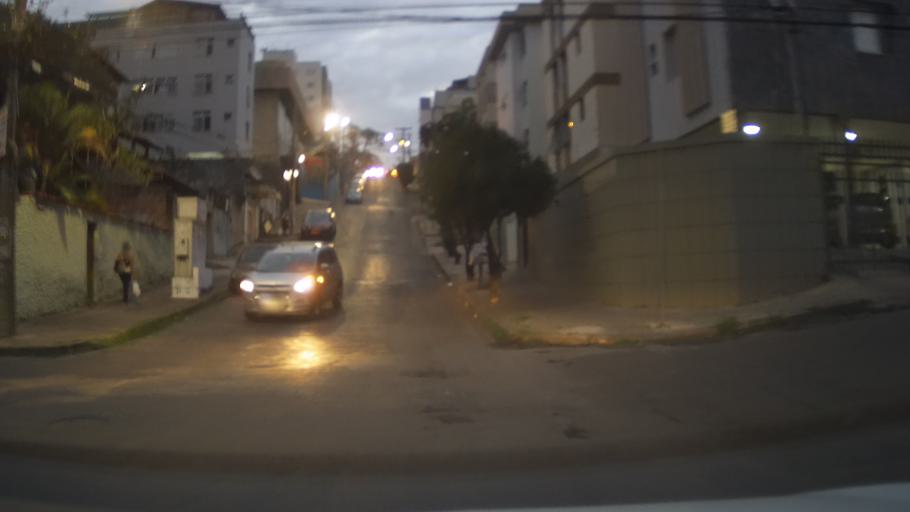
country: BR
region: Minas Gerais
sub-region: Belo Horizonte
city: Belo Horizonte
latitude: -19.8974
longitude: -43.9281
